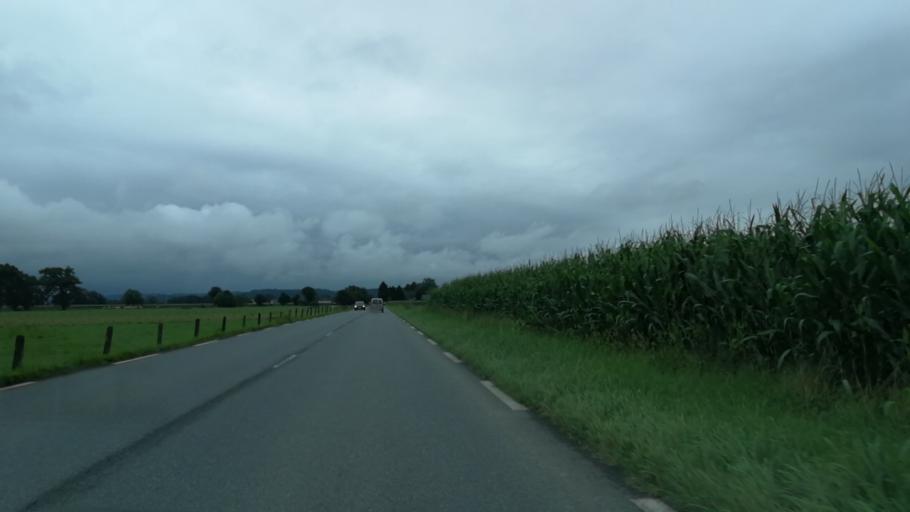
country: FR
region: Aquitaine
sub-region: Departement des Pyrenees-Atlantiques
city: Oloron-Sainte-Marie
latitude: 43.1370
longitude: -0.6058
